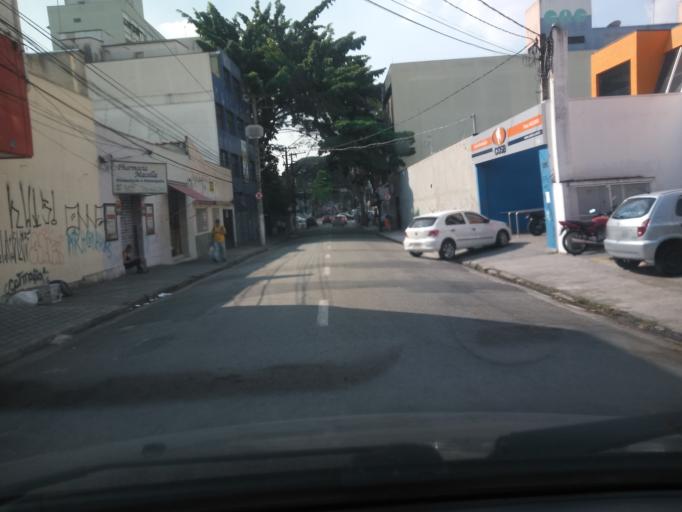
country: BR
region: Sao Paulo
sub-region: Sao Bernardo Do Campo
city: Sao Bernardo do Campo
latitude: -23.7068
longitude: -46.5505
